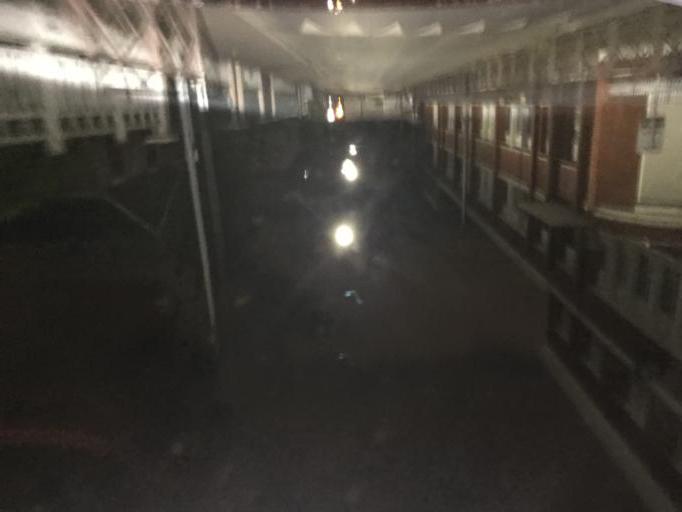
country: FR
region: Ile-de-France
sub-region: Departement des Yvelines
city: Sartrouville
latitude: 48.9432
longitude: 2.1980
